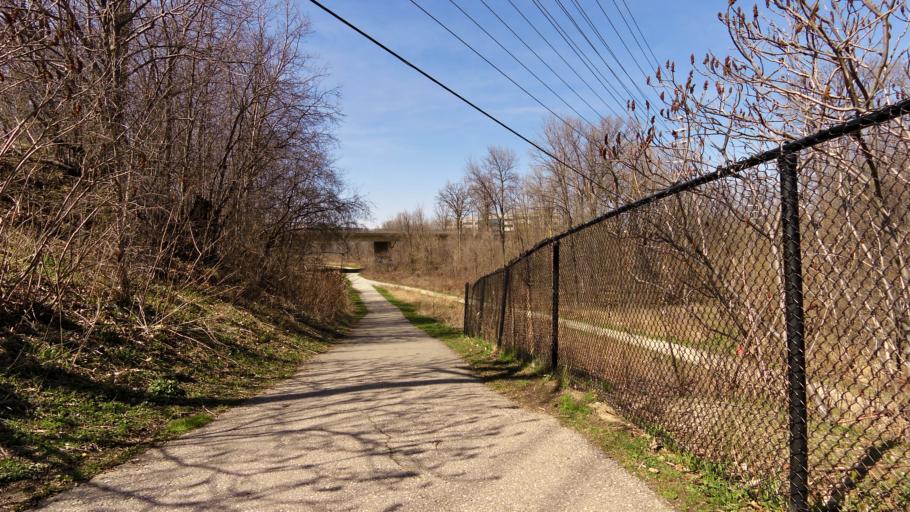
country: CA
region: Ontario
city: Etobicoke
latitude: 43.6500
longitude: -79.6173
